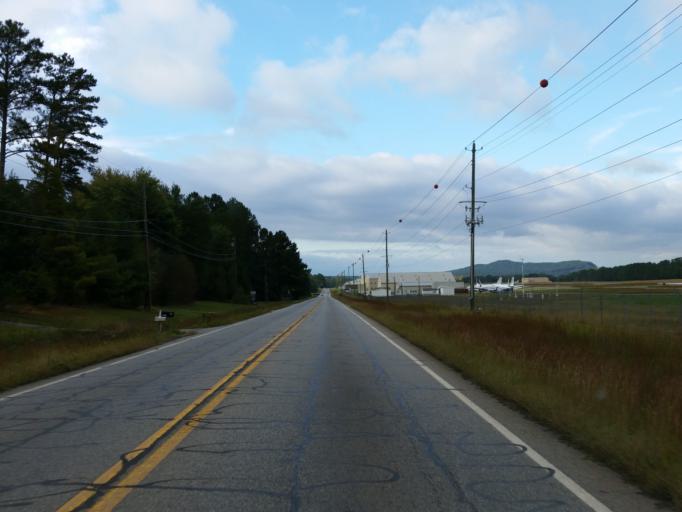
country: US
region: Georgia
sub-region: Bartow County
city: Cartersville
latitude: 34.1146
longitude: -84.8513
